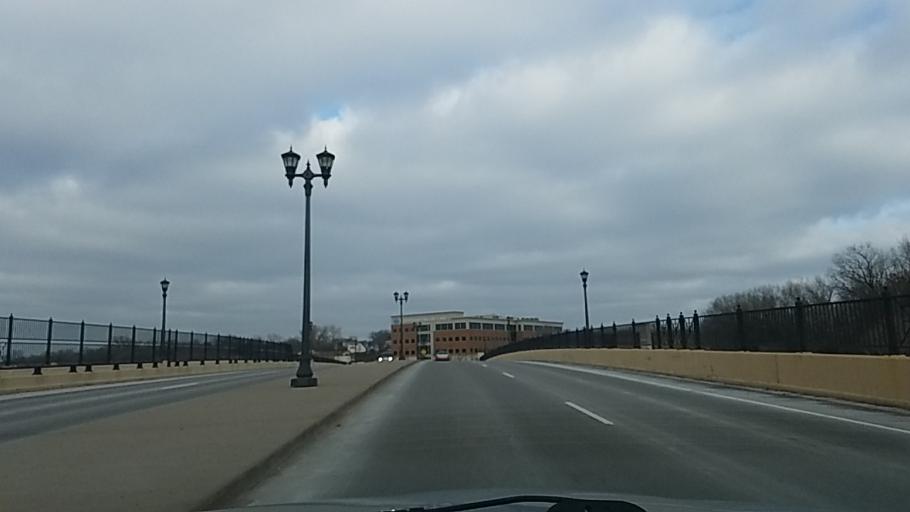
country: US
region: Minnesota
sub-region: Ramsey County
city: Saint Paul
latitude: 44.9620
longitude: -93.0864
